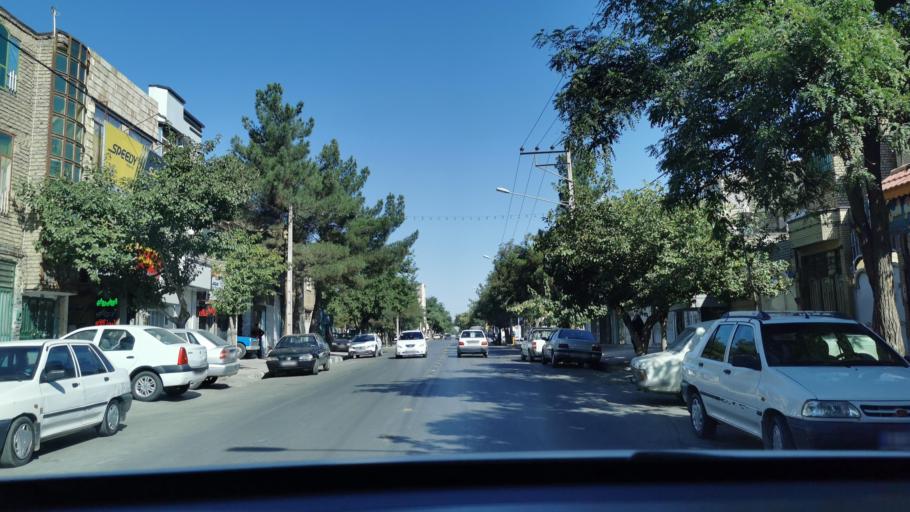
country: IR
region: Razavi Khorasan
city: Mashhad
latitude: 36.3340
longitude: 59.6397
